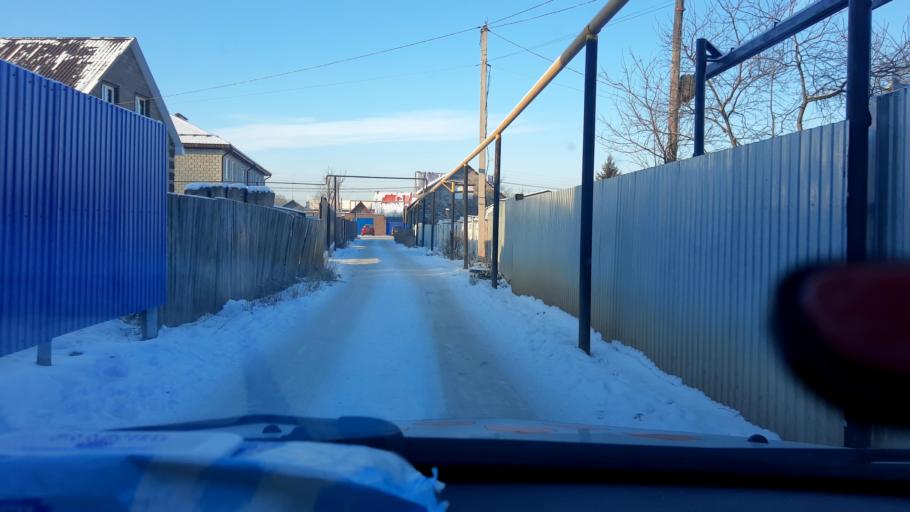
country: RU
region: Bashkortostan
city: Ufa
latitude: 54.7011
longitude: 55.9560
